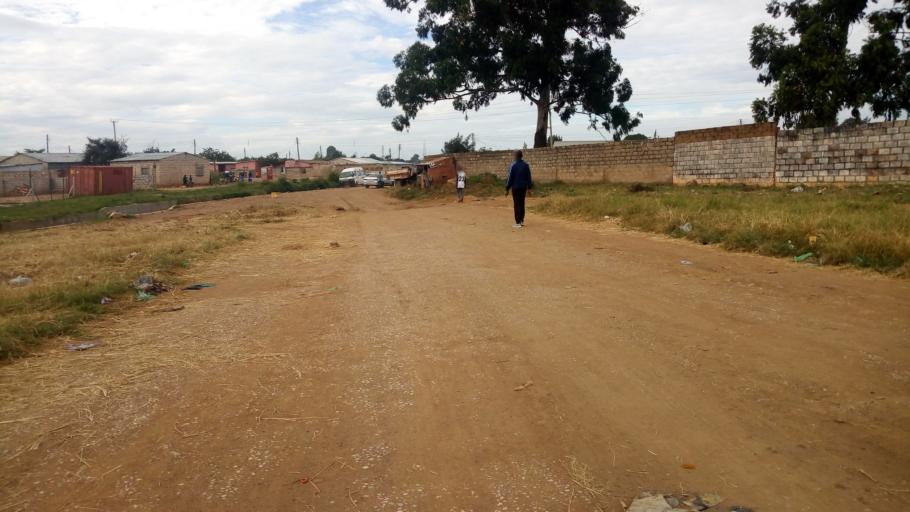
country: ZM
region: Lusaka
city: Lusaka
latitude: -15.3951
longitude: 28.2864
